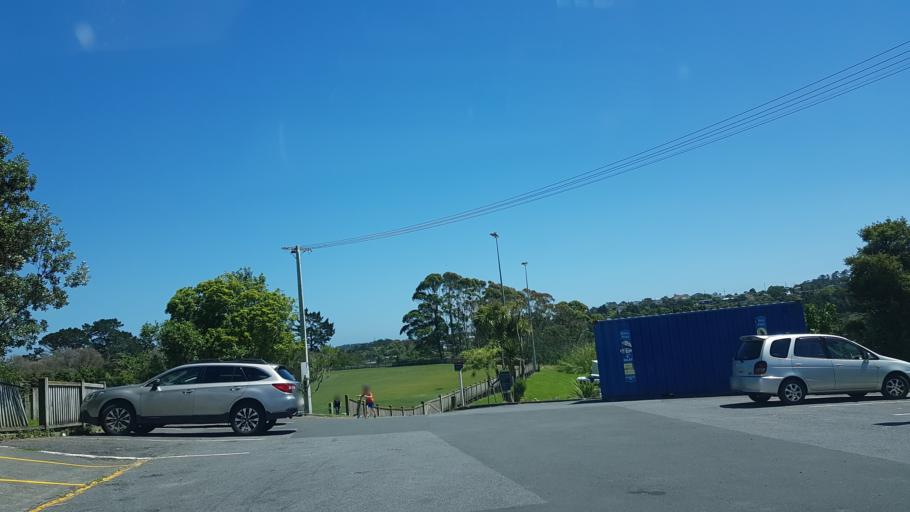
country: NZ
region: Auckland
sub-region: Auckland
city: North Shore
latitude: -36.8072
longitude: 174.7214
